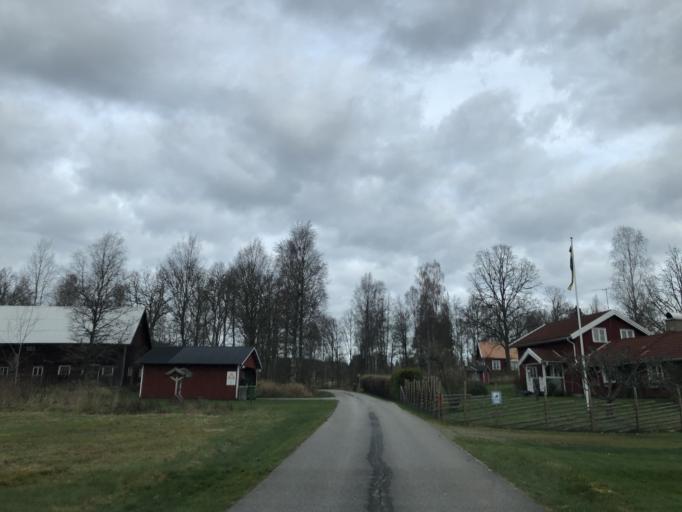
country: SE
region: Vaestra Goetaland
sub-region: Ulricehamns Kommun
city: Ulricehamn
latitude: 57.7326
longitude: 13.3702
